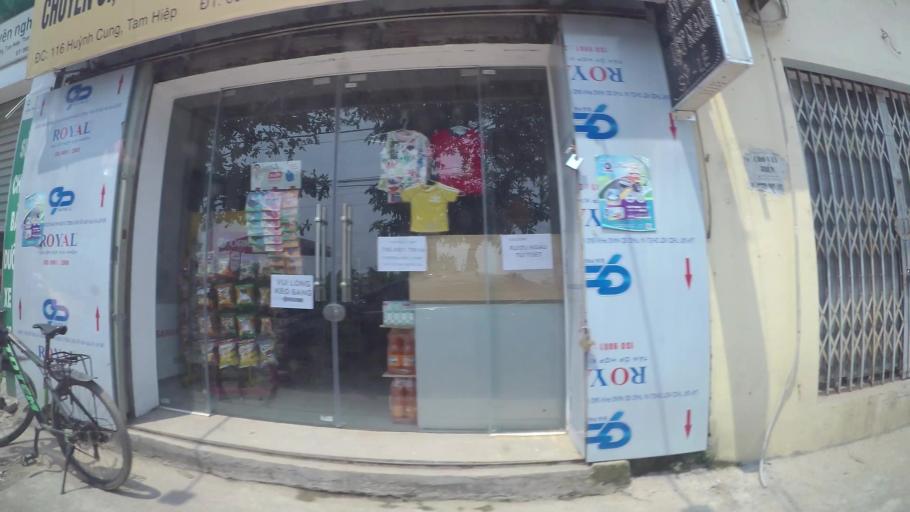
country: VN
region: Ha Noi
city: Van Dien
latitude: 20.9528
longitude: 105.8274
